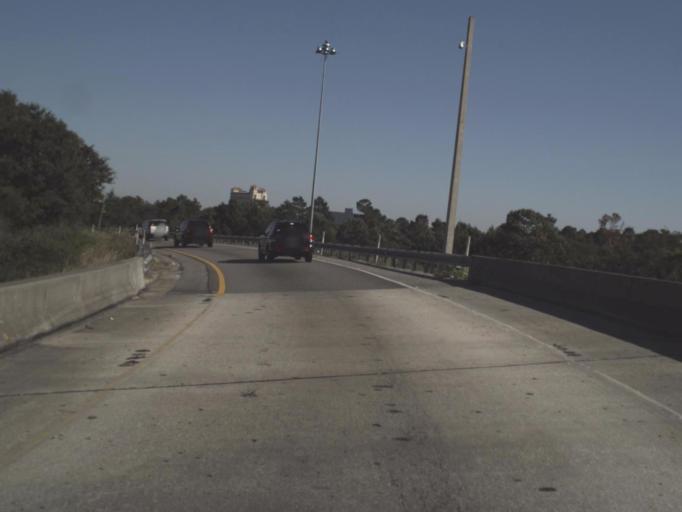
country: US
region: Florida
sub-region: Orange County
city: Williamsburg
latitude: 28.4201
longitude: -81.4741
